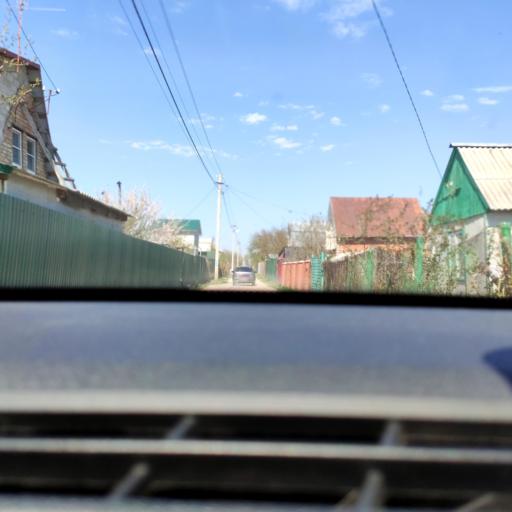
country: RU
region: Samara
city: Tol'yatti
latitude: 53.5938
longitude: 49.3009
